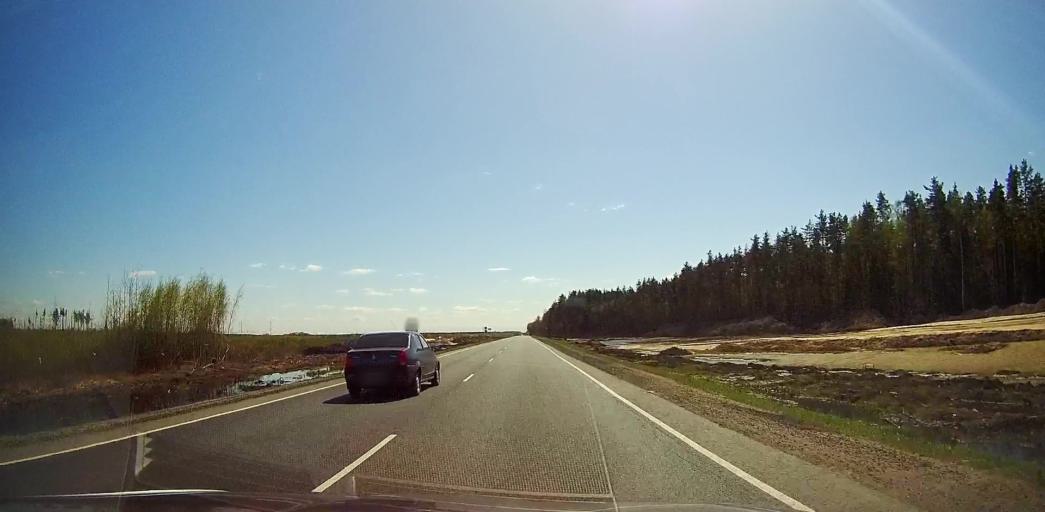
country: RU
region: Moskovskaya
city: Gzhel'
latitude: 55.5952
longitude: 38.3805
